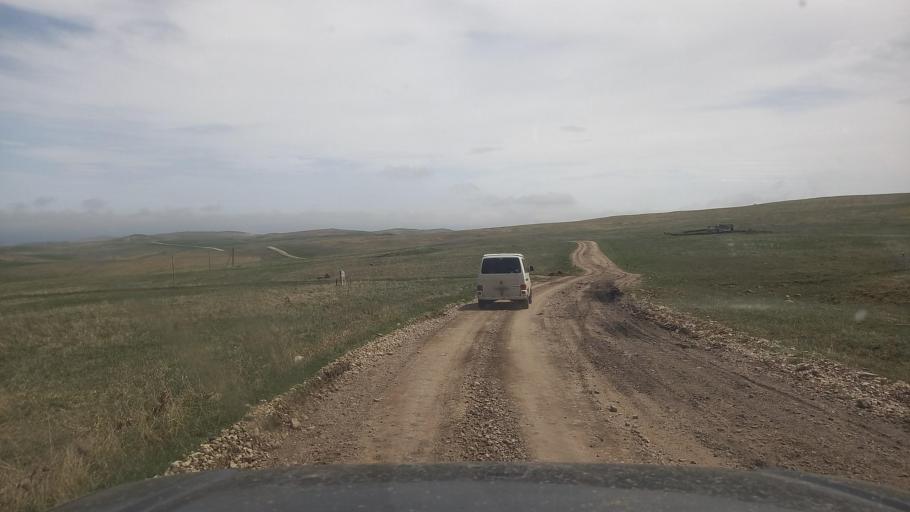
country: RU
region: Stavropol'skiy
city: Kislovodsk
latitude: 43.7595
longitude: 42.7832
